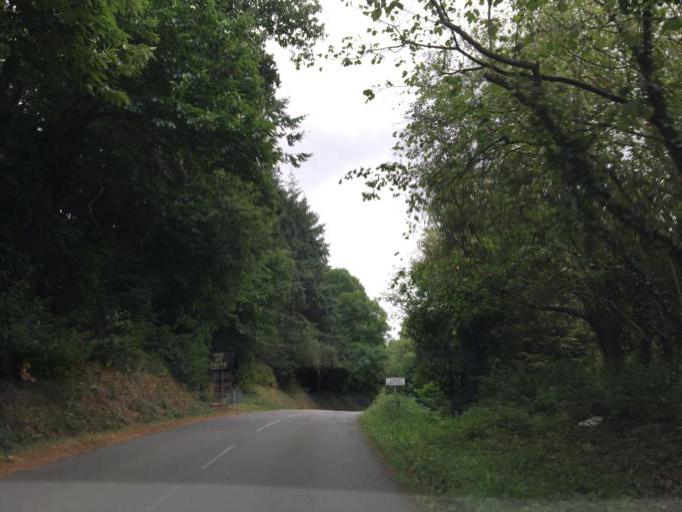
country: FR
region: Brittany
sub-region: Departement des Cotes-d'Armor
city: Jugon-les-Lacs
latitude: 48.4055
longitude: -2.3258
